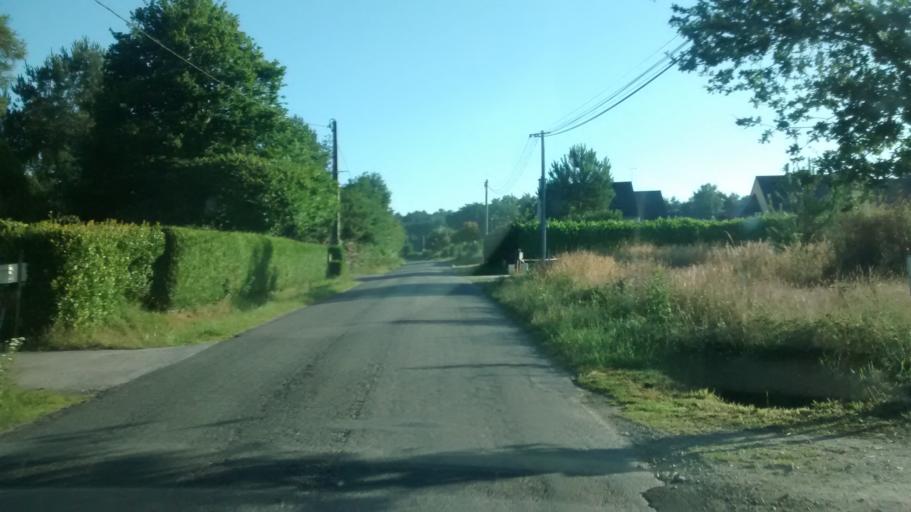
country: FR
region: Brittany
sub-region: Departement du Morbihan
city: Molac
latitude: 47.7375
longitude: -2.4359
